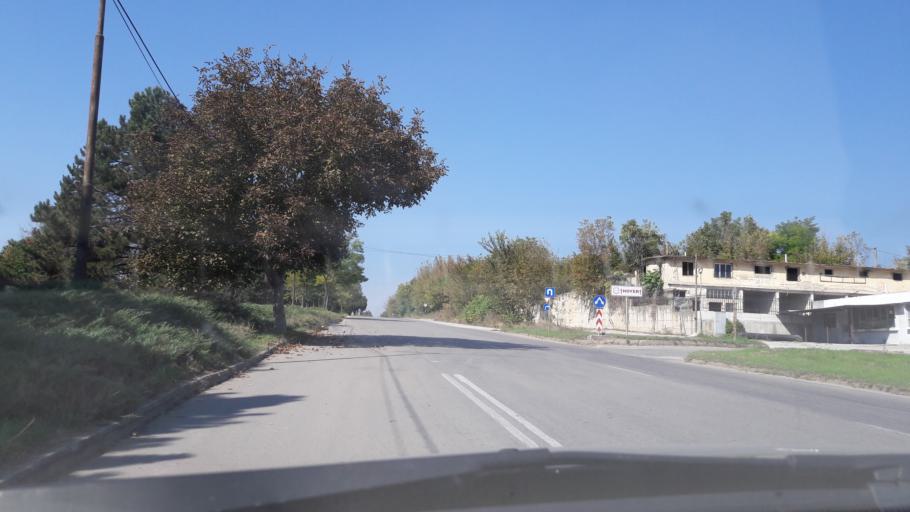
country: BG
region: Razgrad
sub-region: Obshtina Razgrad
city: Razgrad
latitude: 43.5403
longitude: 26.5165
